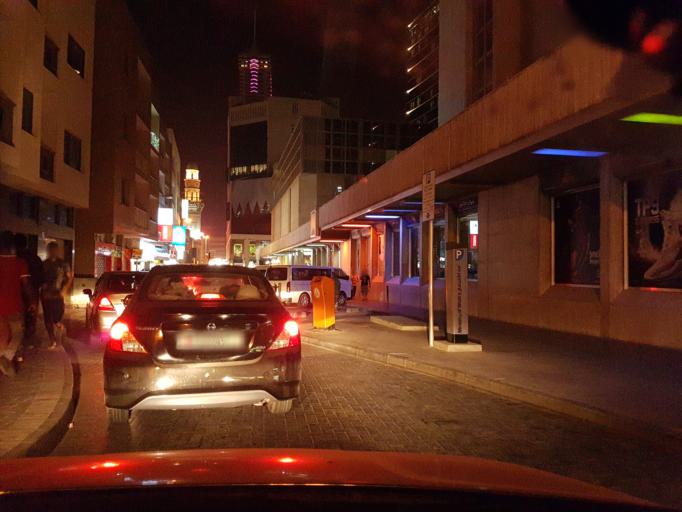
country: BH
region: Manama
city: Manama
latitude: 26.2337
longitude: 50.5774
